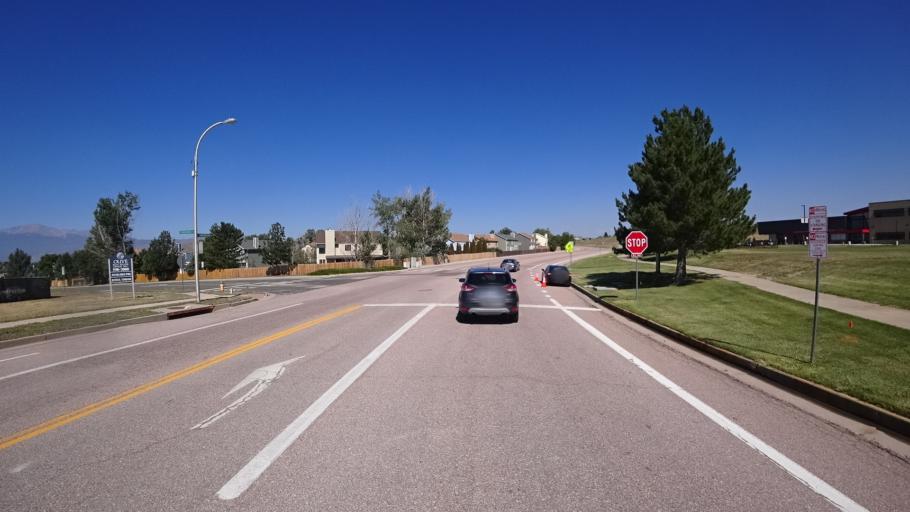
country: US
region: Colorado
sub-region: El Paso County
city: Black Forest
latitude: 38.9580
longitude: -104.7374
